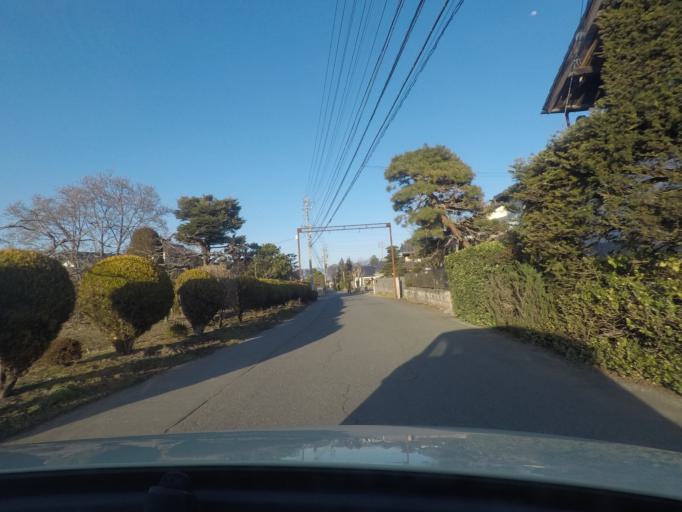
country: JP
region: Nagano
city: Matsumoto
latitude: 36.2115
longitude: 137.8869
